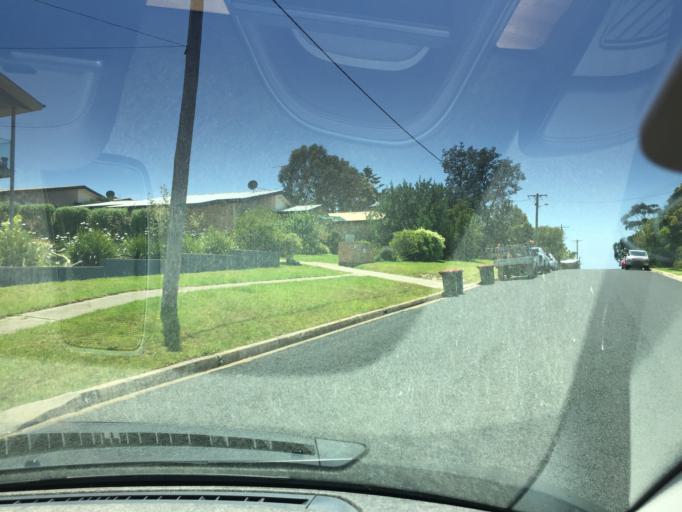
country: AU
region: New South Wales
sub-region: Bega Valley
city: Bega
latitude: -36.7339
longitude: 149.9806
